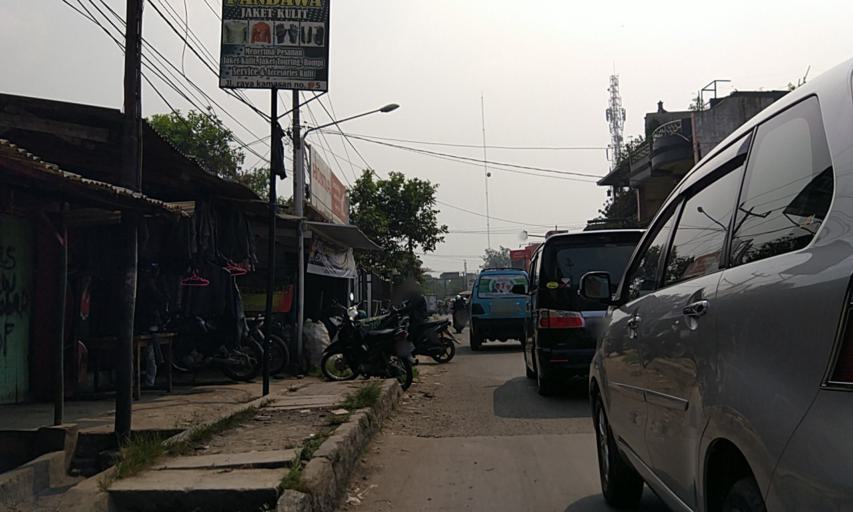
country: ID
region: West Java
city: Banjaran
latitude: -7.0472
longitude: 107.5809
